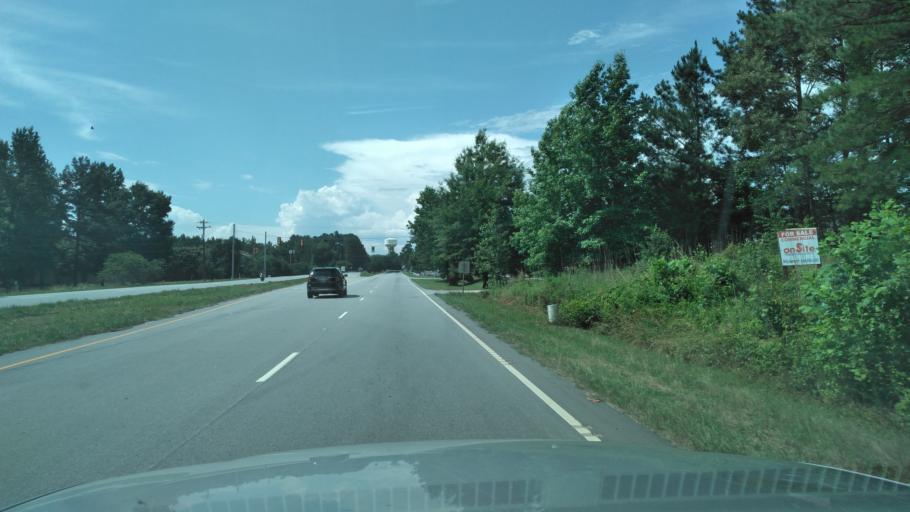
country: US
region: South Carolina
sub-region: Spartanburg County
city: Roebuck
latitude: 34.8824
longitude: -81.9567
